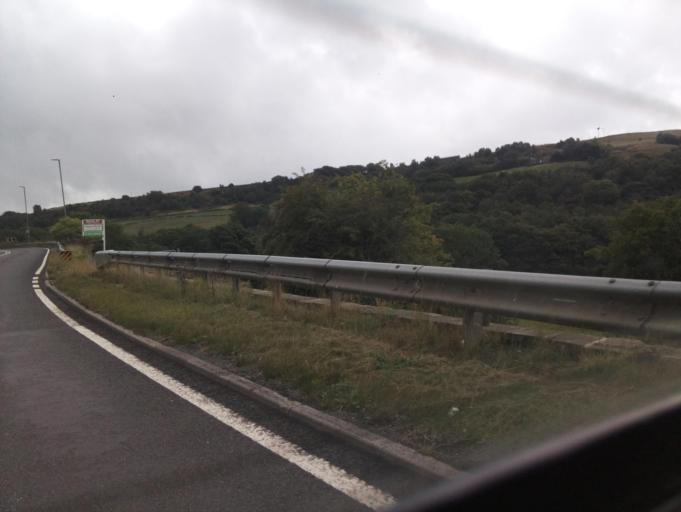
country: GB
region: England
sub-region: Kirklees
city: Kirkburton
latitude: 53.5731
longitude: -1.7369
